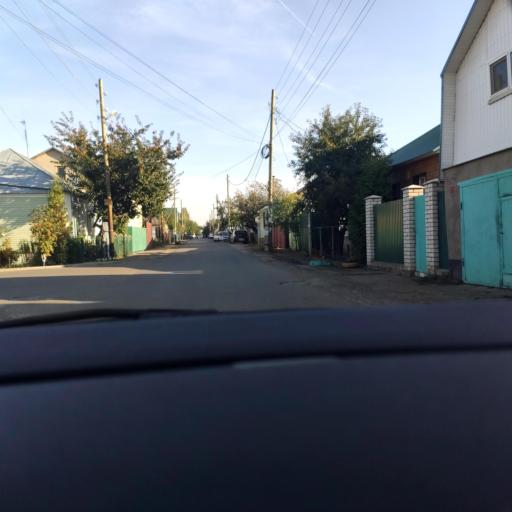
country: RU
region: Voronezj
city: Voronezh
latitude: 51.6289
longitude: 39.1694
